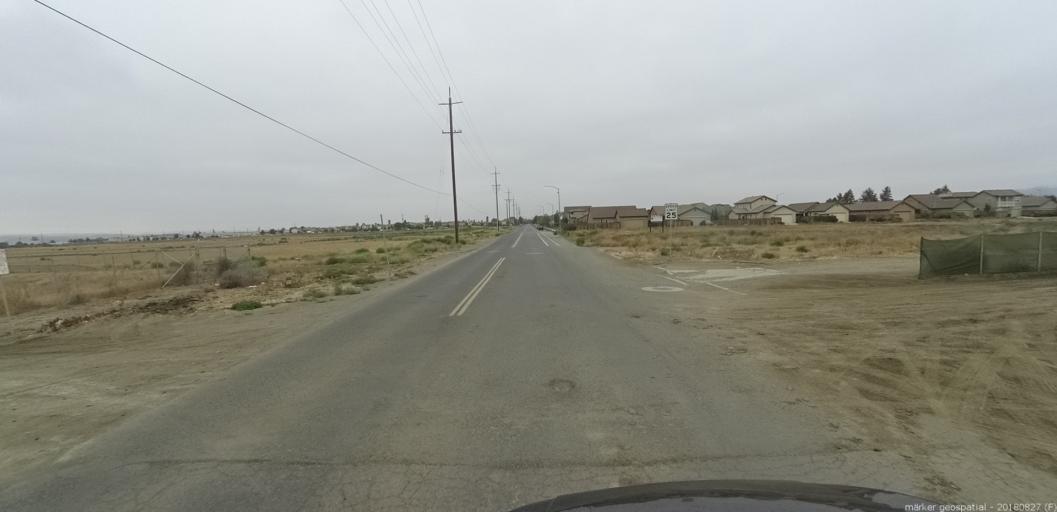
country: US
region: California
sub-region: Monterey County
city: King City
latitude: 36.2247
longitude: -121.1363
